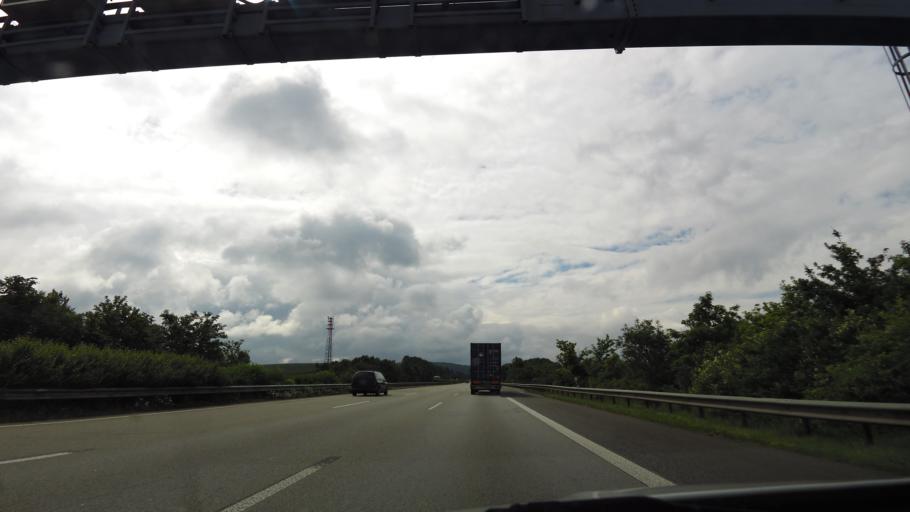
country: DE
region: Rheinland-Pfalz
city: Wehr
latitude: 50.4260
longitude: 7.2279
